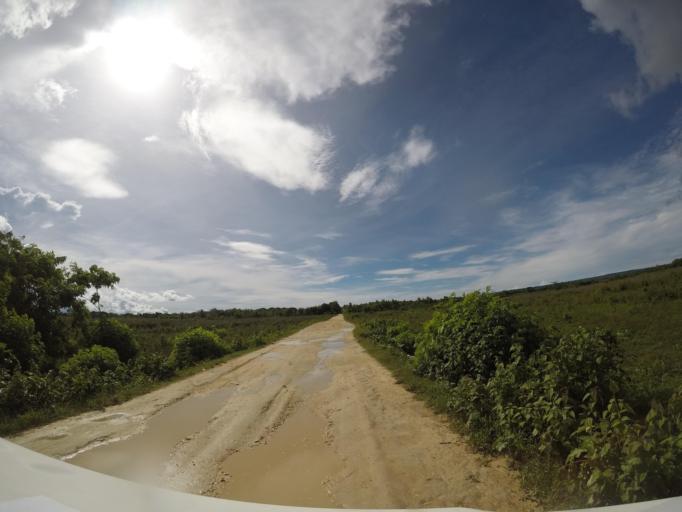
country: TL
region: Lautem
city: Lospalos
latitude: -8.5029
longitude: 127.0061
